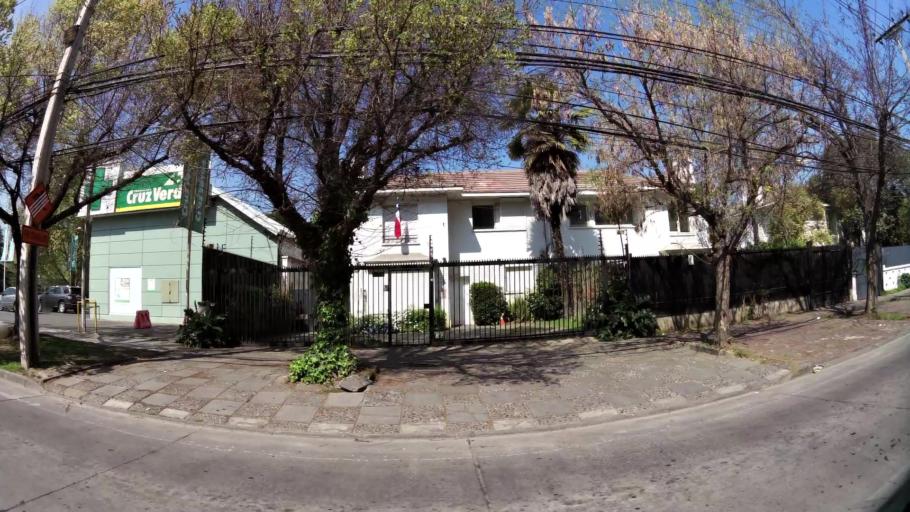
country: CL
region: Santiago Metropolitan
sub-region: Provincia de Santiago
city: Villa Presidente Frei, Nunoa, Santiago, Chile
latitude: -33.3930
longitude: -70.5931
